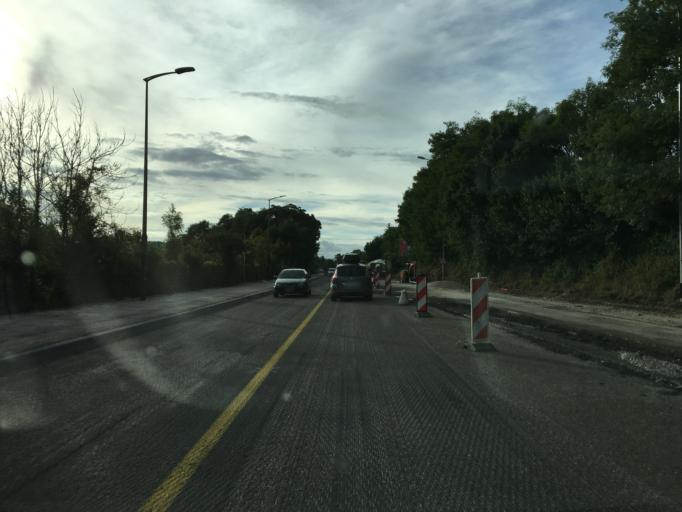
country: FR
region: Bourgogne
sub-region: Departement de la Cote-d'Or
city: Talant
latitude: 47.3310
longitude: 4.9934
